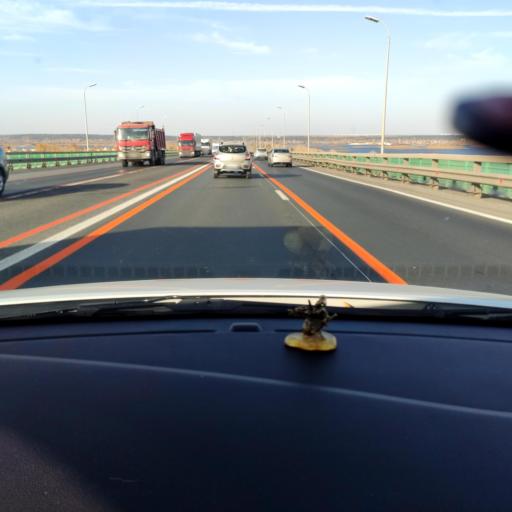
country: RU
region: Tatarstan
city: Osinovo
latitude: 55.7865
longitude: 48.8399
